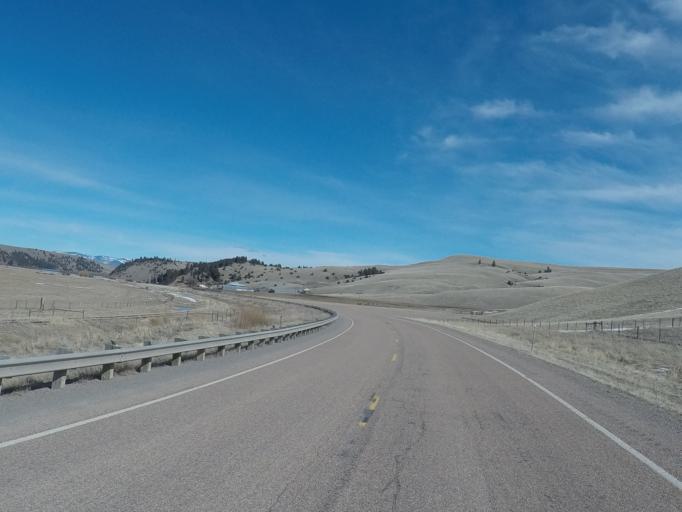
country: US
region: Montana
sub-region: Granite County
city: Philipsburg
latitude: 46.4936
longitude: -113.2224
